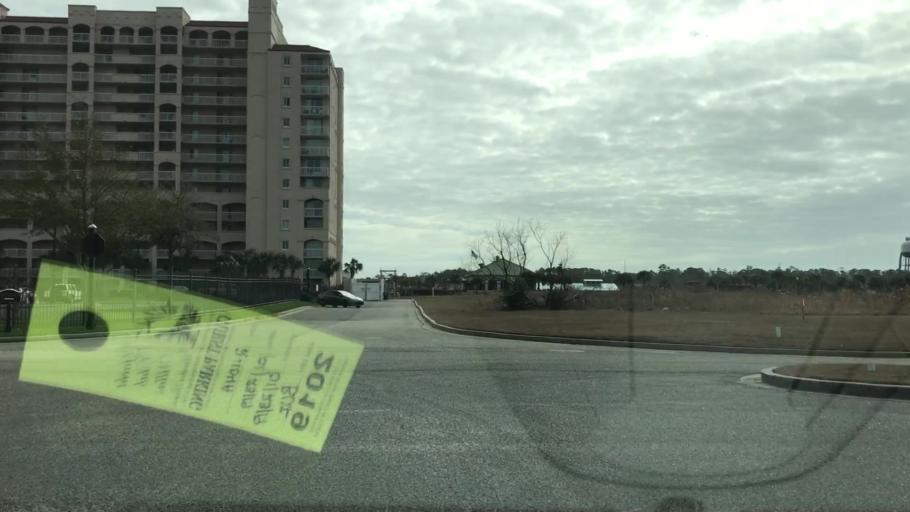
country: US
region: South Carolina
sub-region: Horry County
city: North Myrtle Beach
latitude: 33.8045
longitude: -78.7475
